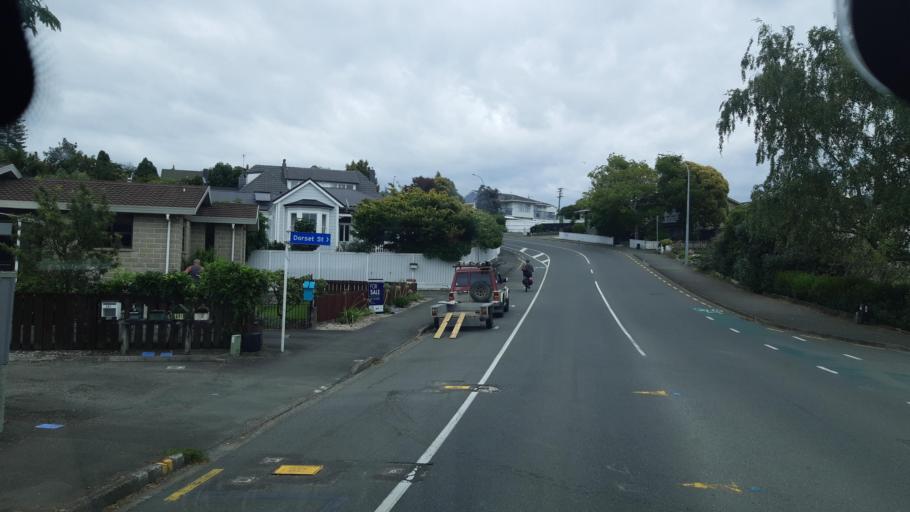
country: NZ
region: Tasman
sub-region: Tasman District
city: Richmond
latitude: -41.3423
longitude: 173.1841
